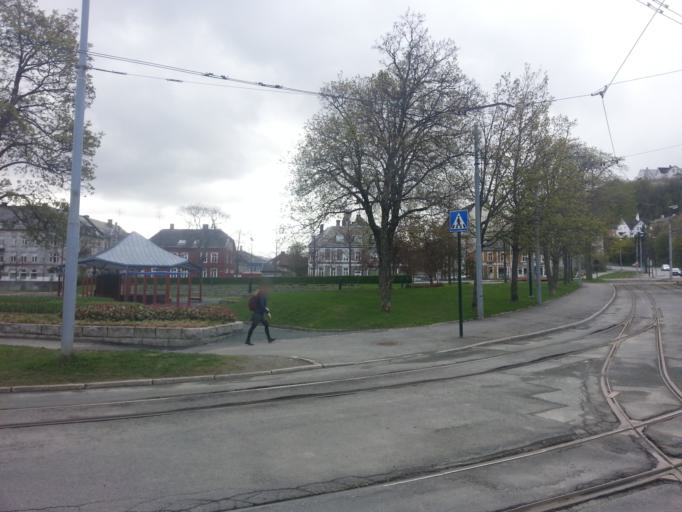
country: NO
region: Sor-Trondelag
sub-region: Trondheim
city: Trondheim
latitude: 63.4292
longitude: 10.3672
